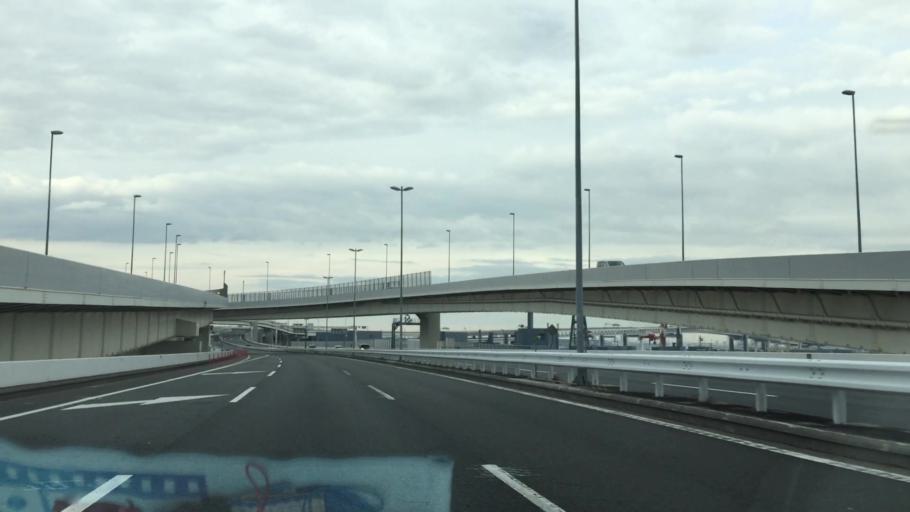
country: JP
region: Kanagawa
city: Yokohama
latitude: 35.4344
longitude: 139.6674
